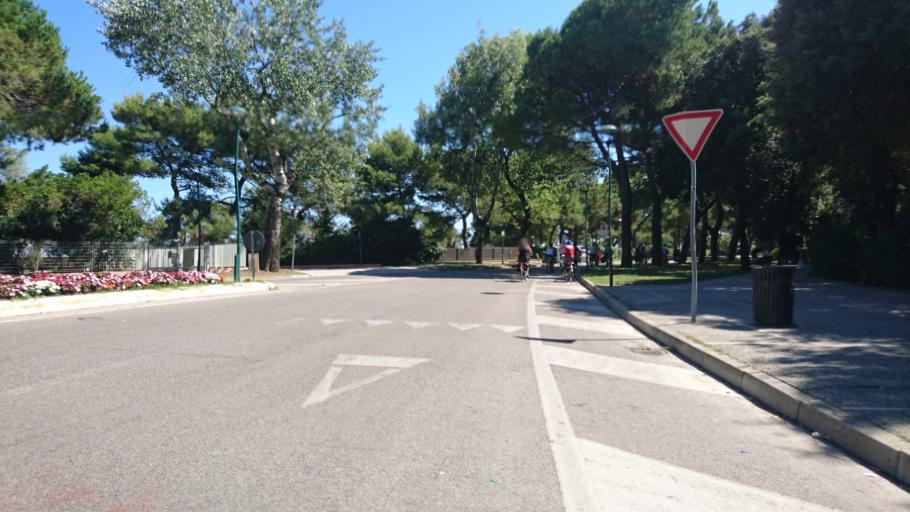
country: IT
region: Veneto
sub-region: Provincia di Venezia
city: Lido
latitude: 45.4144
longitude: 12.3760
